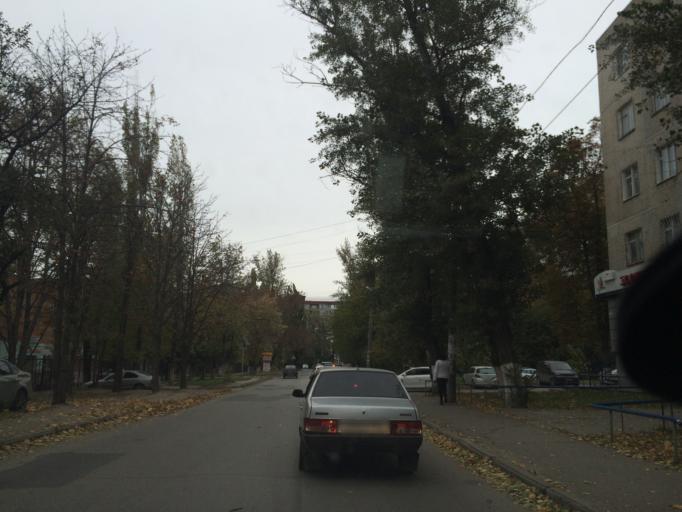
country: RU
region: Rostov
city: Rostov-na-Donu
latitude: 47.2104
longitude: 39.6232
